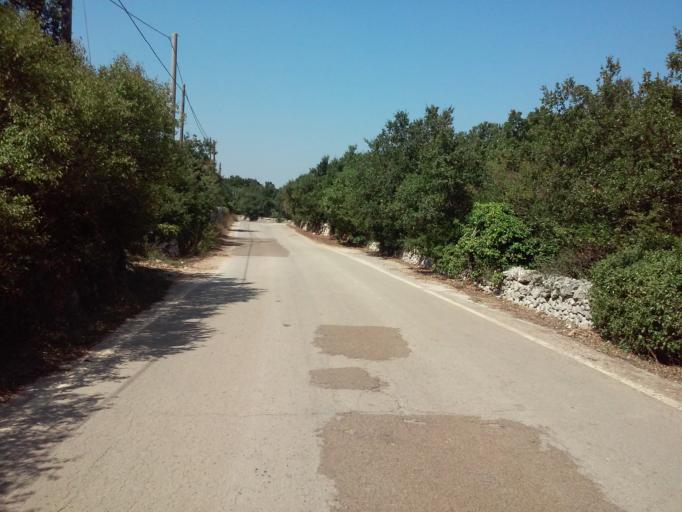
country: IT
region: Apulia
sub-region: Provincia di Bari
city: Alberobello
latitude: 40.8036
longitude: 17.2084
